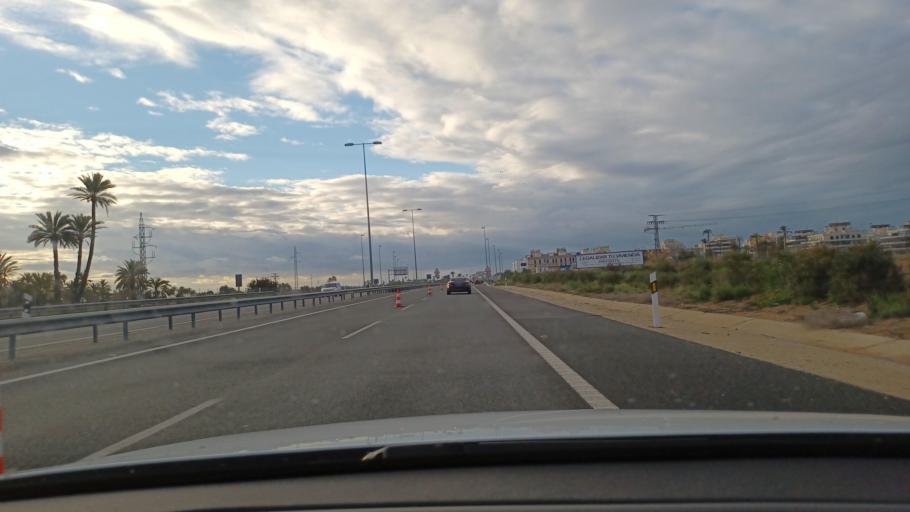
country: ES
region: Valencia
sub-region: Provincia de Alicante
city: Elche
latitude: 38.2690
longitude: -0.6605
